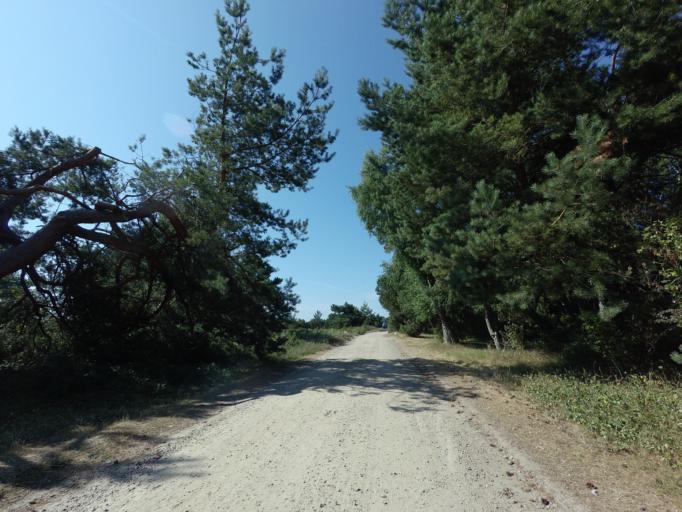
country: SE
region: Skane
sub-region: Vellinge Kommun
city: Ljunghusen
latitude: 55.3924
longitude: 12.9323
